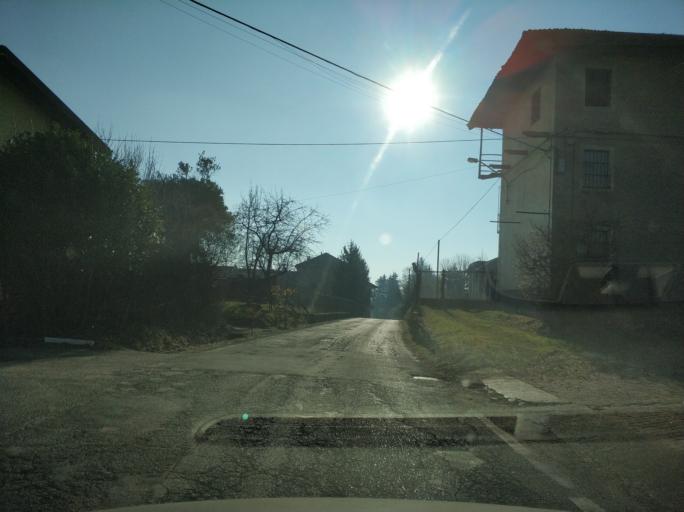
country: IT
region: Piedmont
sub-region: Provincia di Torino
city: Rocca Canavese
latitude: 45.2980
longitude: 7.5800
